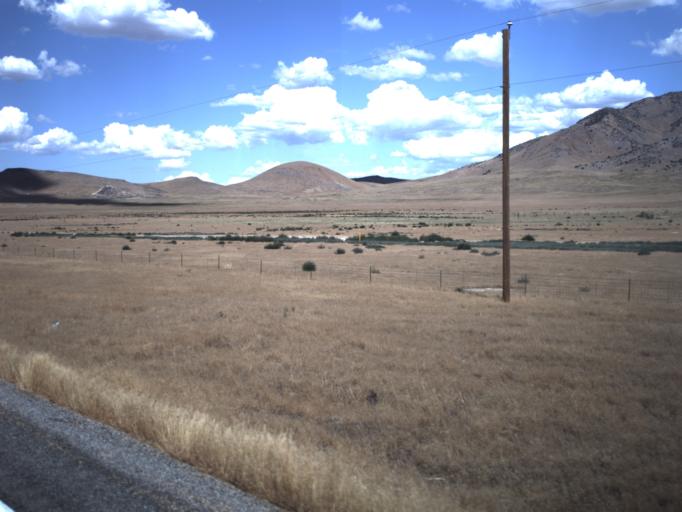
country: US
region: Utah
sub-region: Millard County
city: Delta
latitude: 39.6311
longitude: -112.3092
